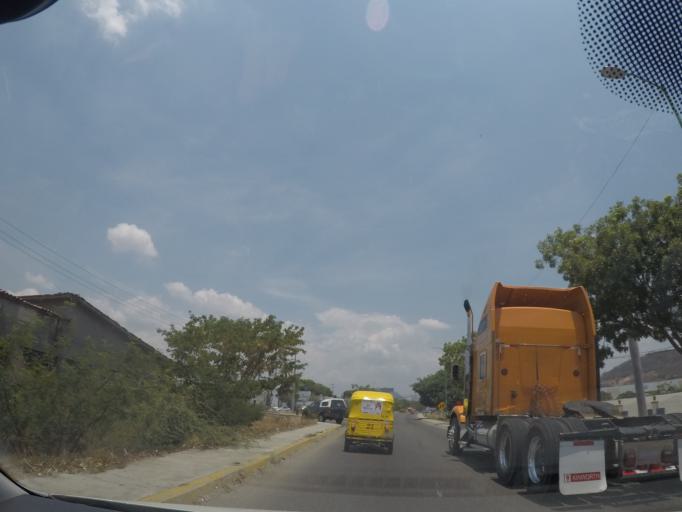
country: MX
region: Oaxaca
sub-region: Santo Domingo Tehuantepec
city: Santo Domingo Tehuantepec
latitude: 16.3242
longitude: -95.2414
